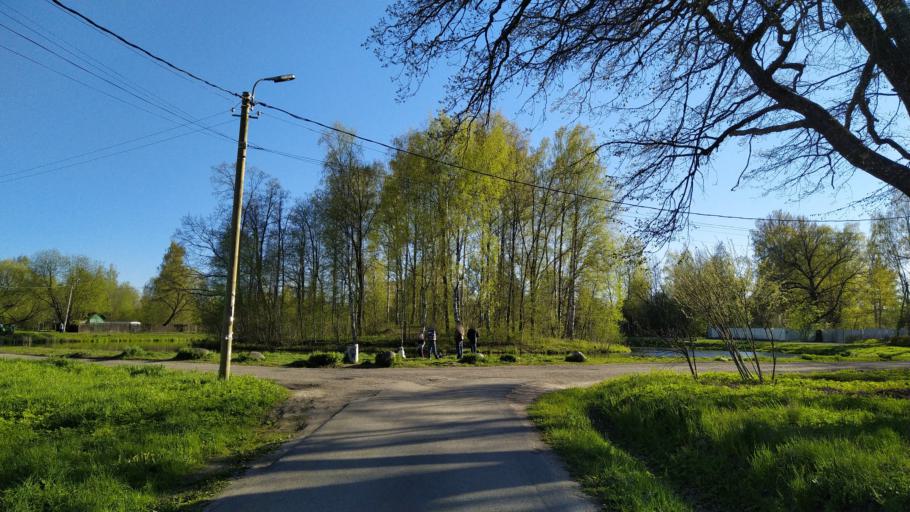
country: RU
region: St.-Petersburg
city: Tyarlevo
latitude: 59.6793
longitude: 30.4626
